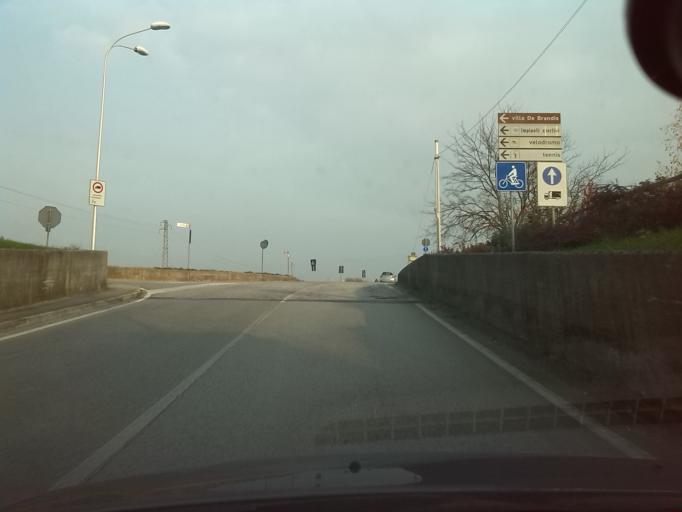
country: IT
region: Friuli Venezia Giulia
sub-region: Provincia di Udine
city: San Giovanni al Natisone
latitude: 45.9708
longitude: 13.4087
